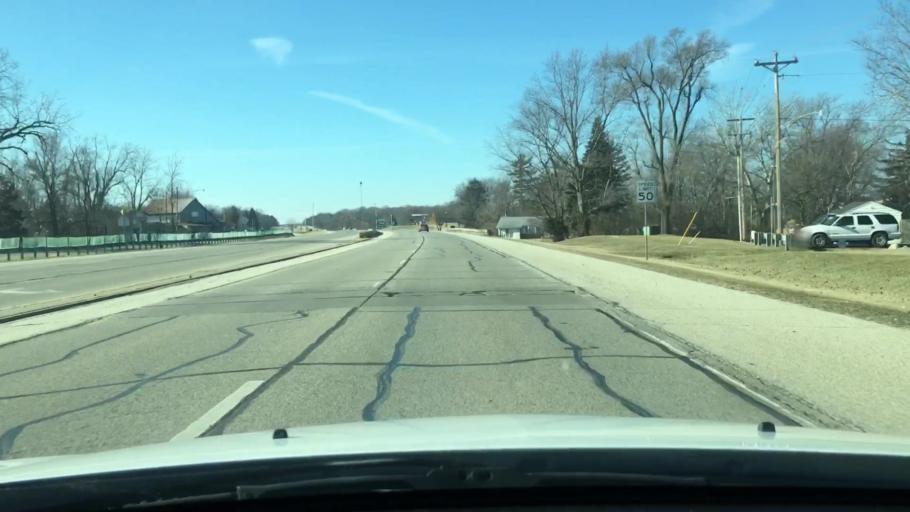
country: US
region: Illinois
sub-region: Woodford County
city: Germantown Hills
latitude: 40.7665
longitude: -89.4676
